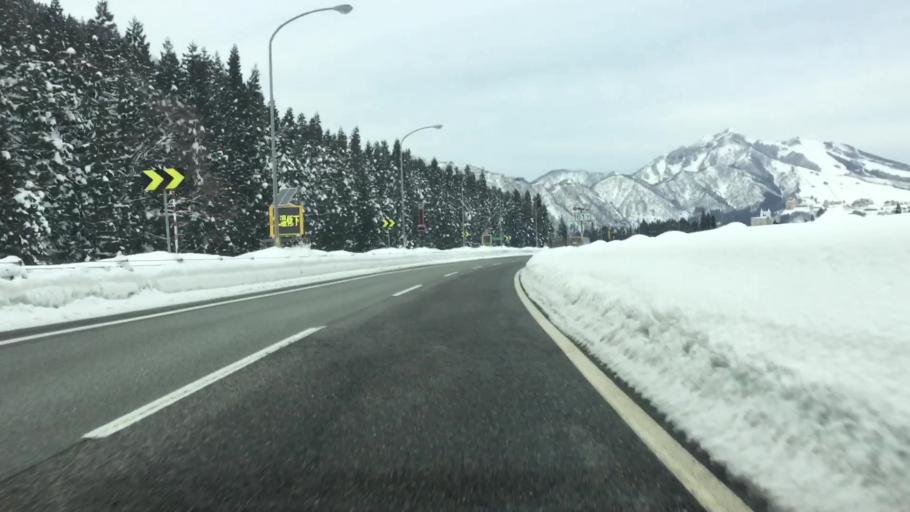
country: JP
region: Niigata
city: Shiozawa
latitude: 36.8931
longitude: 138.8459
